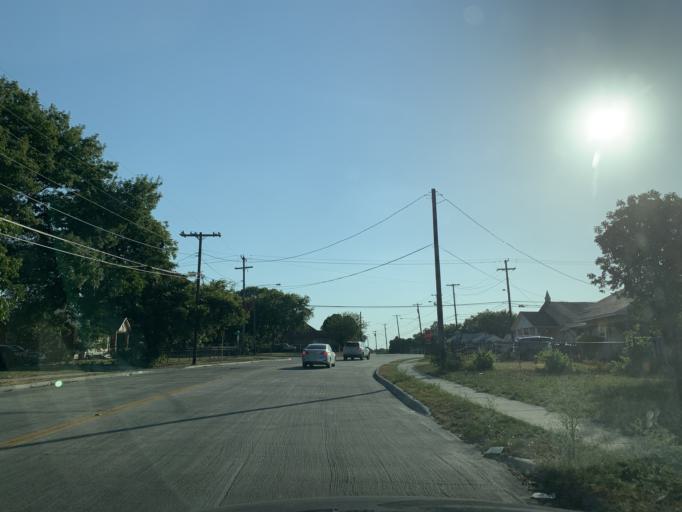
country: US
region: Texas
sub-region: Dallas County
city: Dallas
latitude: 32.7063
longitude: -96.7955
